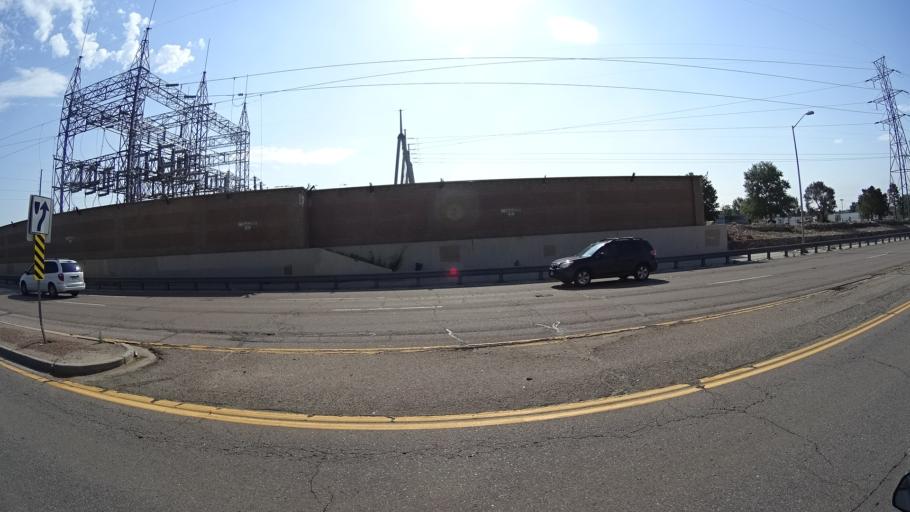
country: US
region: Colorado
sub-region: El Paso County
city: Stratmoor
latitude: 38.7921
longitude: -104.7577
